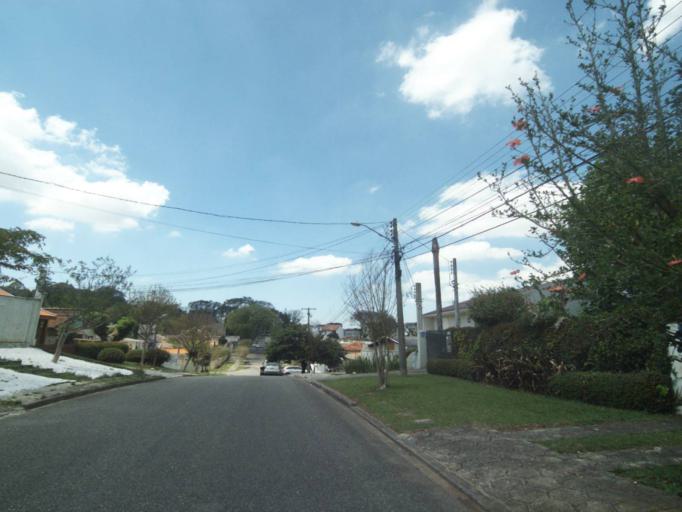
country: BR
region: Parana
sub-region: Curitiba
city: Curitiba
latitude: -25.4089
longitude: -49.2356
